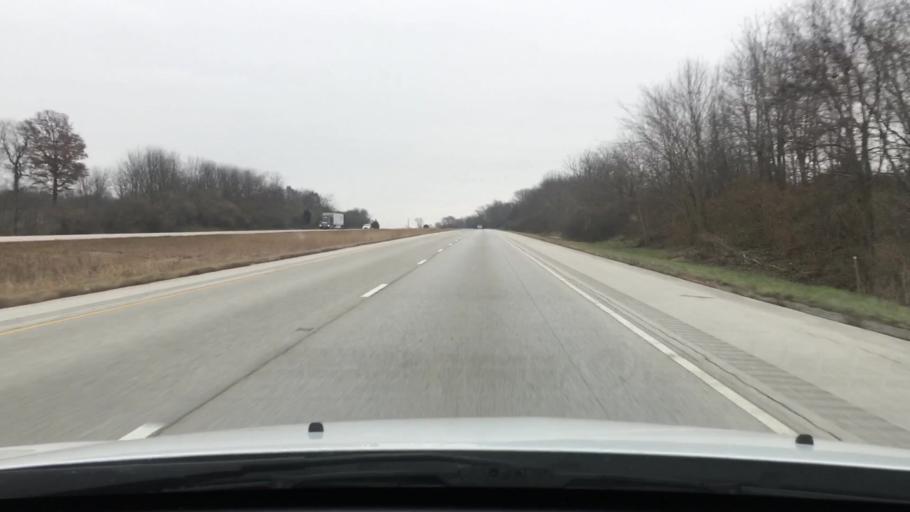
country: US
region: Illinois
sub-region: Scott County
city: Winchester
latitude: 39.6807
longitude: -90.3915
